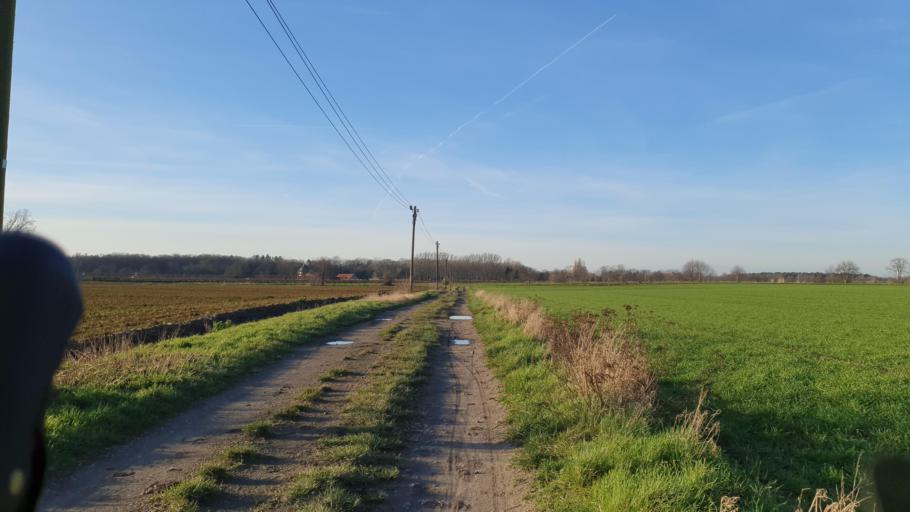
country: DE
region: North Rhine-Westphalia
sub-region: Regierungsbezirk Koln
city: Sinnersdorf
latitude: 51.0471
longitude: 6.8262
